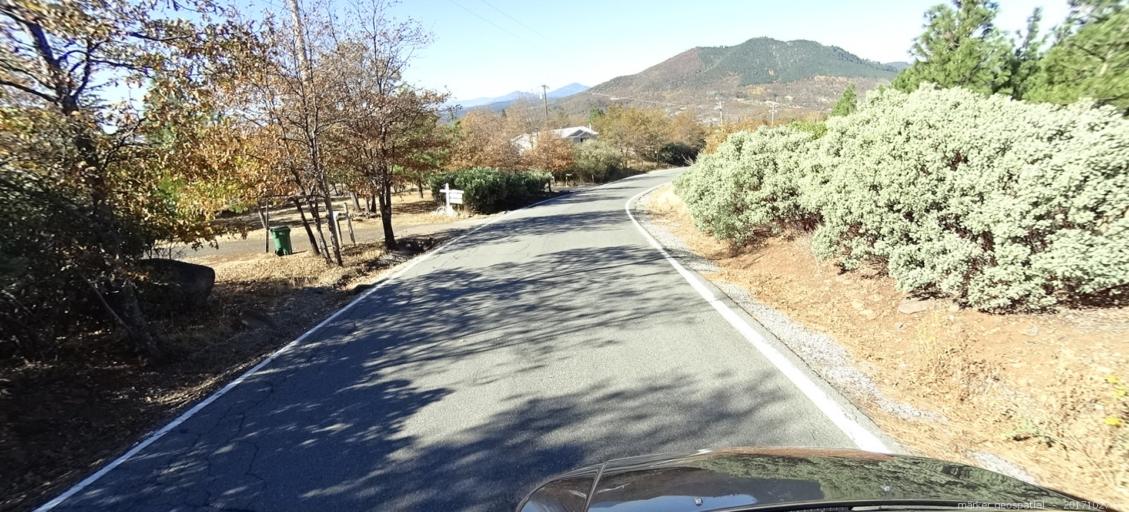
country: US
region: California
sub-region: Shasta County
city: Burney
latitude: 40.7906
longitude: -121.9199
